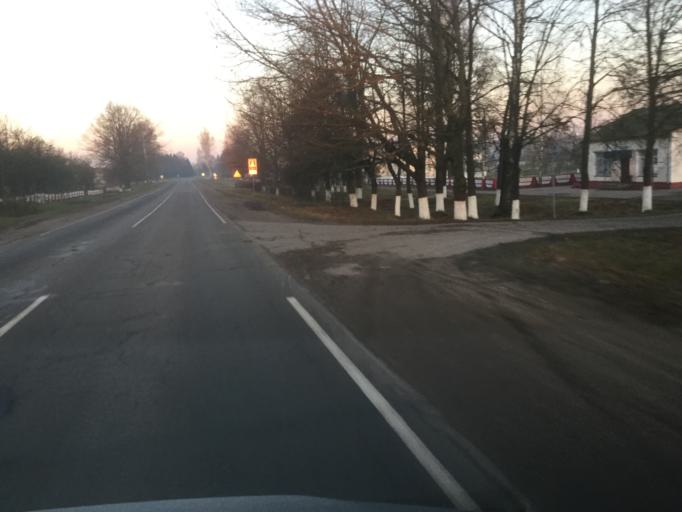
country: BY
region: Vitebsk
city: Vyerkhnyadzvinsk
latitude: 55.7101
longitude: 28.0869
